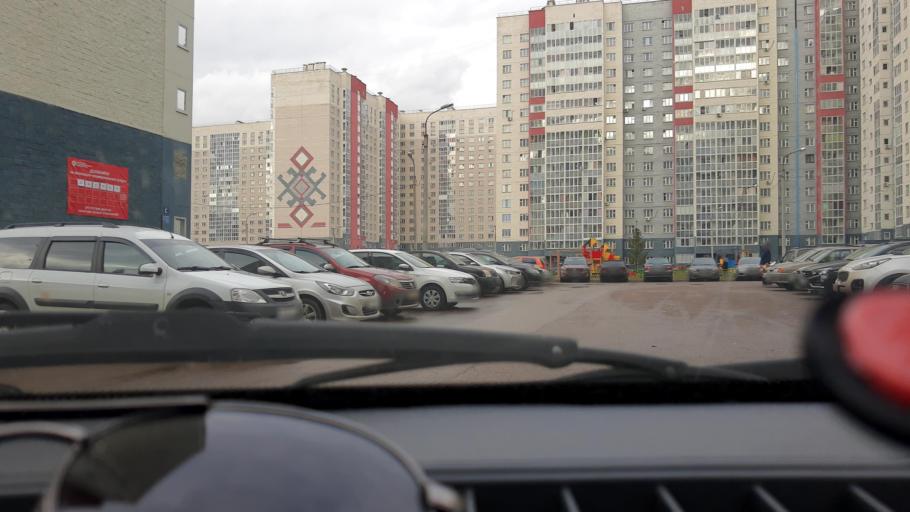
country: RU
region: Bashkortostan
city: Ufa
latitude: 54.7850
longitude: 56.1373
